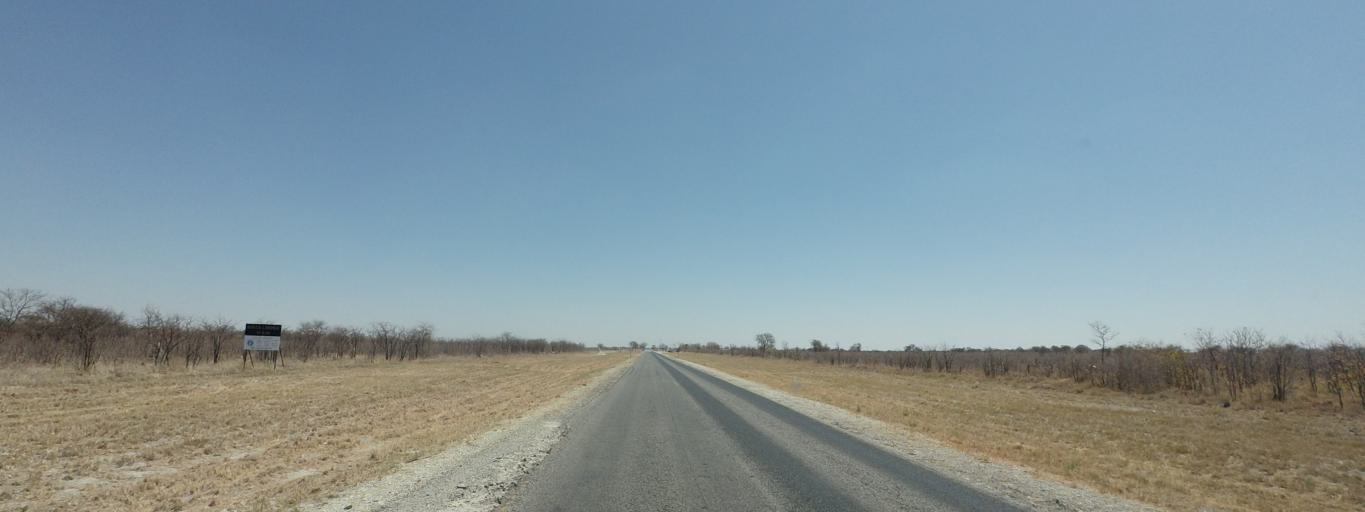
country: BW
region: Central
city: Nata
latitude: -20.3198
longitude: 26.3094
